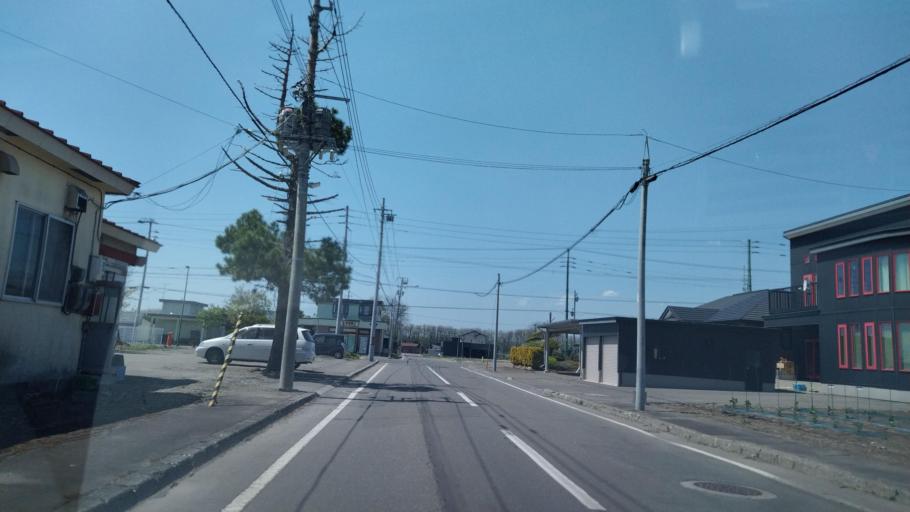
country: JP
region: Hokkaido
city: Otofuke
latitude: 43.1625
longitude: 143.2454
